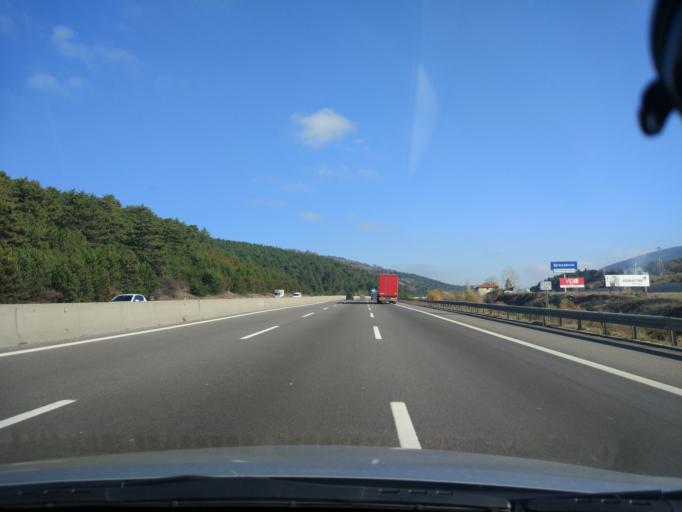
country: TR
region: Bolu
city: Gokcesu
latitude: 40.7377
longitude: 31.8199
